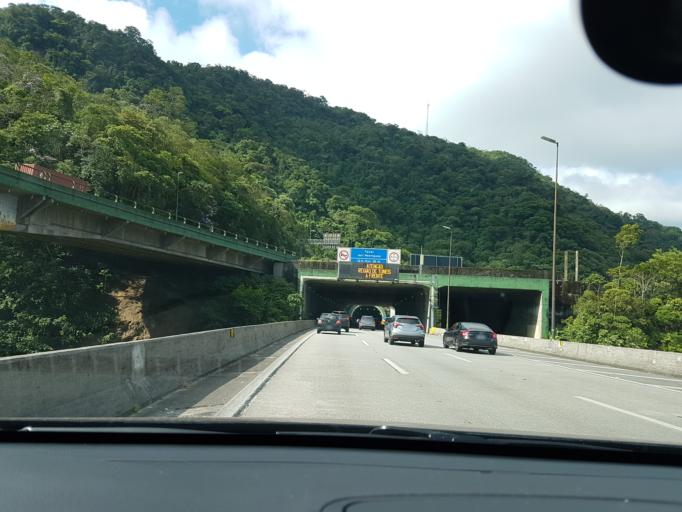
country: BR
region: Sao Paulo
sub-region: Cubatao
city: Cubatao
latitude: -23.9197
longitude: -46.5311
